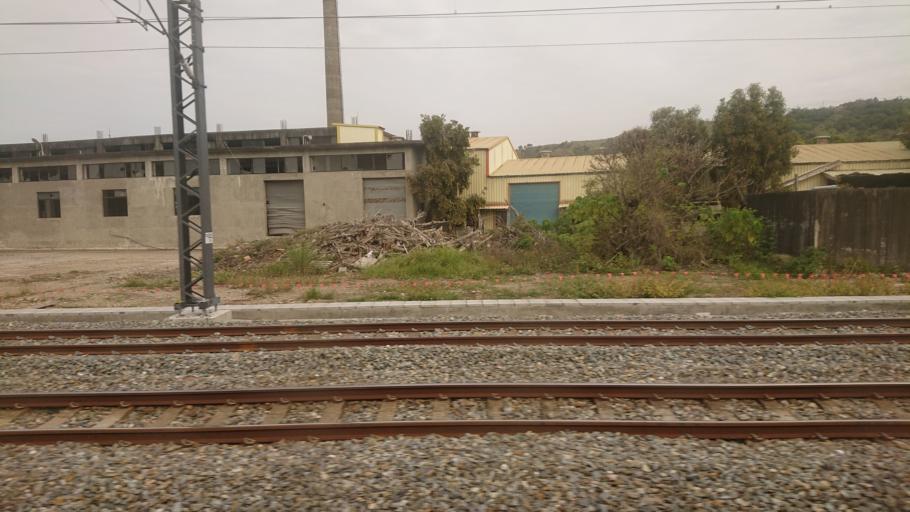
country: TW
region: Taiwan
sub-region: Changhua
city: Chang-hua
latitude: 24.1159
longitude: 120.5851
